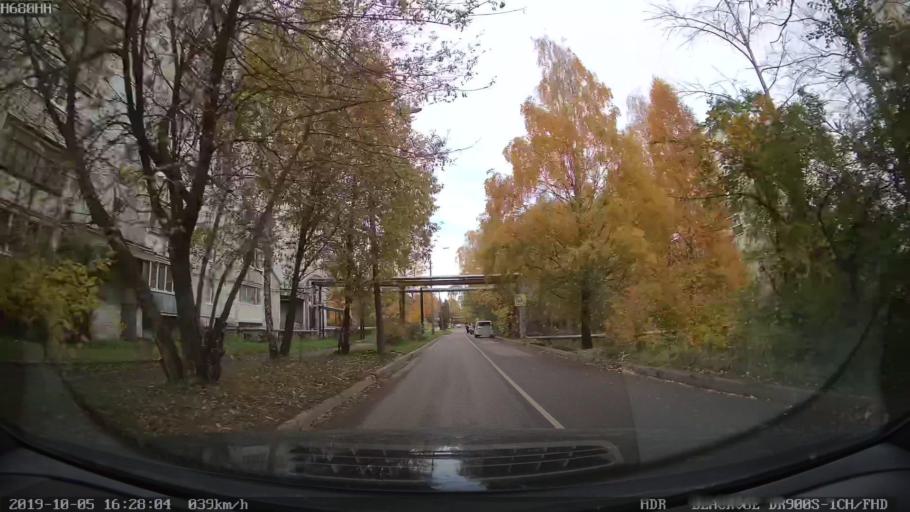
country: RU
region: Moskovskaya
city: Solnechnogorsk
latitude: 56.2146
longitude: 37.0281
